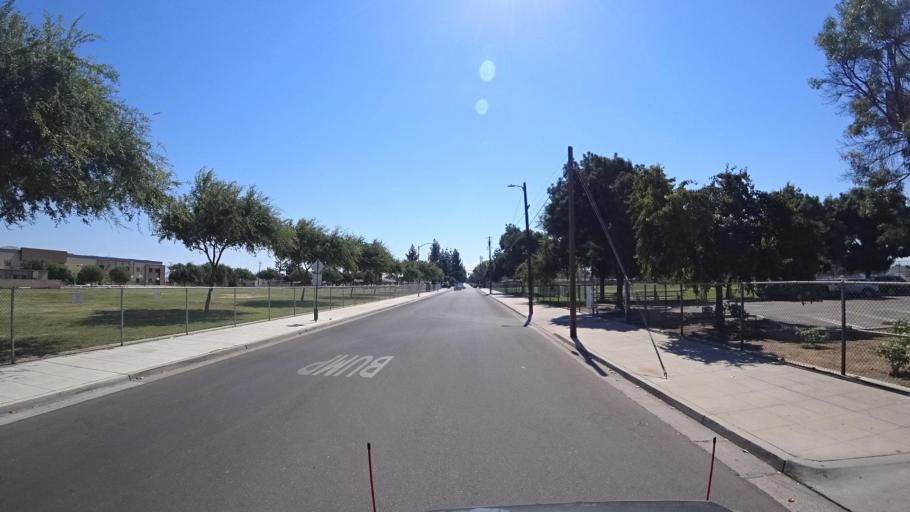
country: US
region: California
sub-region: Fresno County
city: Fresno
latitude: 36.7250
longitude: -119.7564
